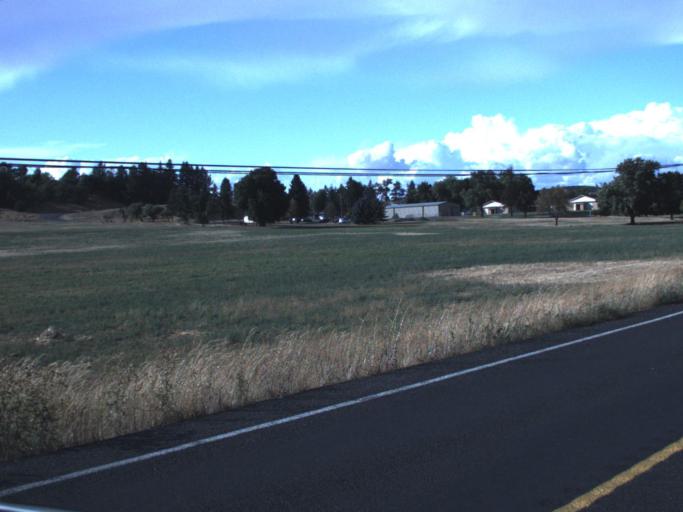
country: US
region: Washington
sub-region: Spokane County
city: Medical Lake
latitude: 47.5465
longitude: -117.7045
